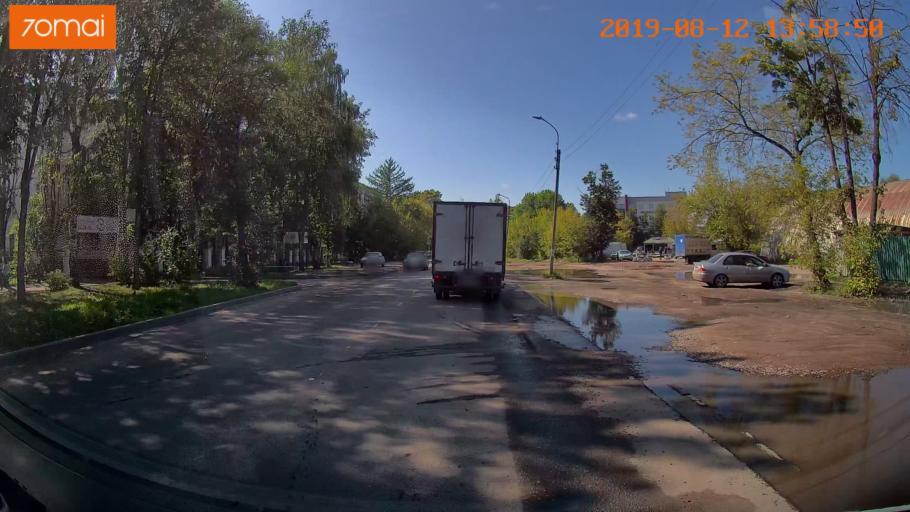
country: RU
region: Ivanovo
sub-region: Gorod Ivanovo
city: Ivanovo
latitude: 57.0024
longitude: 40.9467
